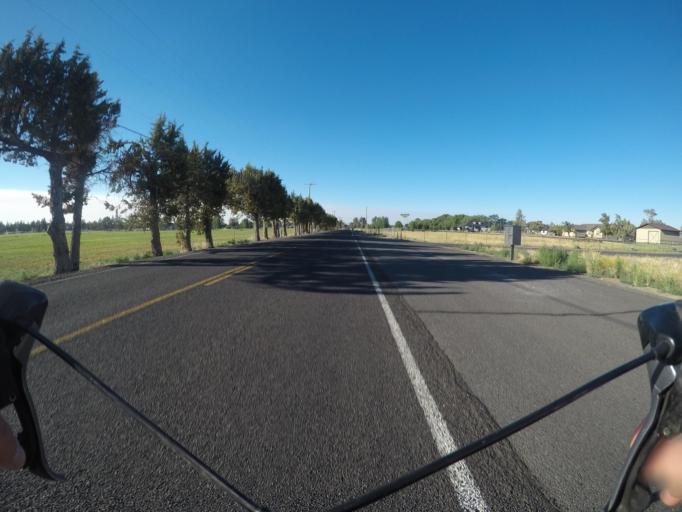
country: US
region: Oregon
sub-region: Deschutes County
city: Redmond
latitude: 44.2460
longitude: -121.2396
